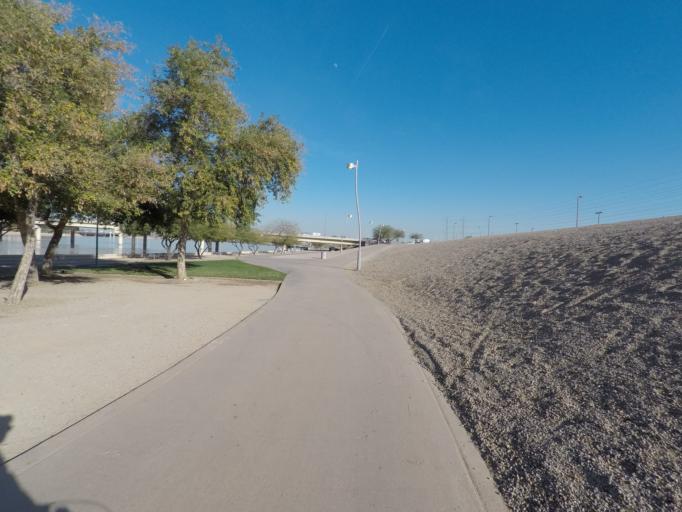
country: US
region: Arizona
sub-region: Maricopa County
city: Tempe Junction
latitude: 33.4300
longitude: -111.9281
